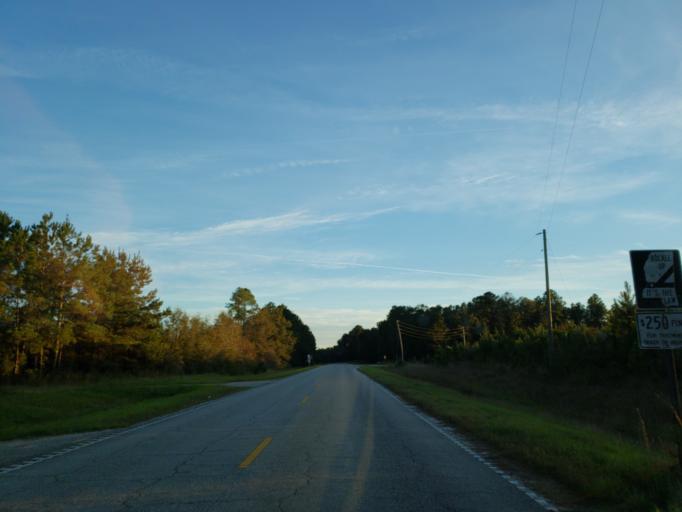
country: US
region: Mississippi
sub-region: Wayne County
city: Belmont
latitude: 31.4169
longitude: -88.4710
